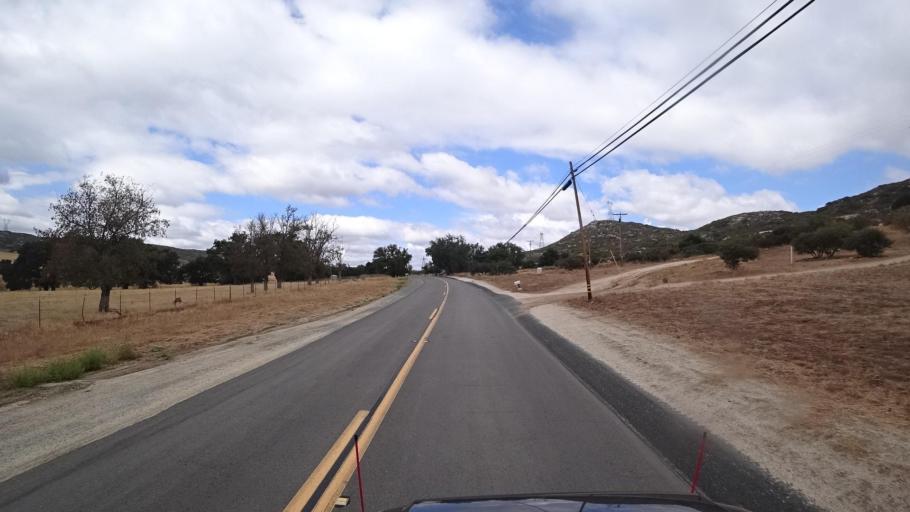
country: US
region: California
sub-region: San Diego County
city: Campo
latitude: 32.6539
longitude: -116.4966
